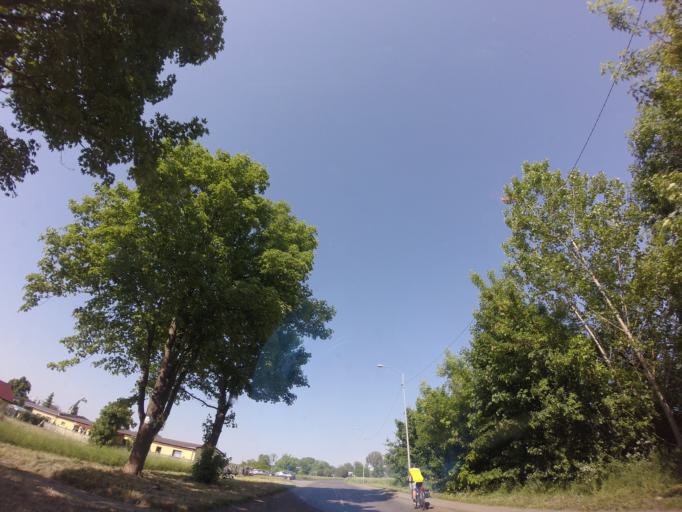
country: PL
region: West Pomeranian Voivodeship
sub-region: Powiat gryfinski
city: Stare Czarnowo
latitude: 53.3027
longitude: 14.8178
